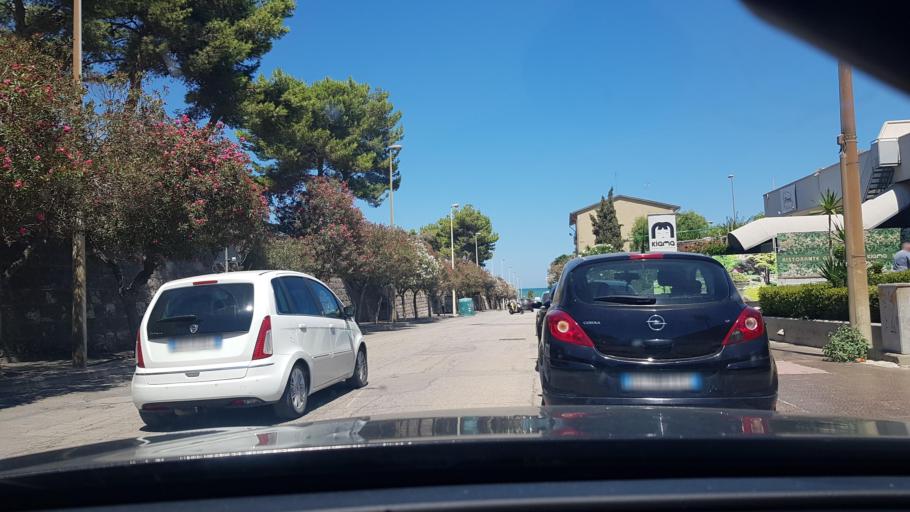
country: IT
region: Apulia
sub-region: Provincia di Barletta - Andria - Trani
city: Barletta
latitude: 41.3173
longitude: 16.2983
